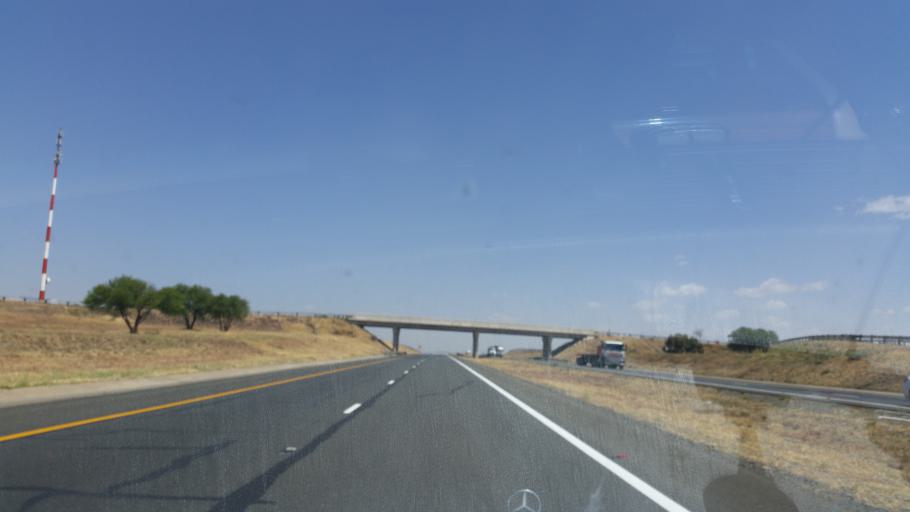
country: ZA
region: Orange Free State
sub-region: Lejweleputswa District Municipality
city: Brandfort
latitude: -28.9330
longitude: 26.4223
